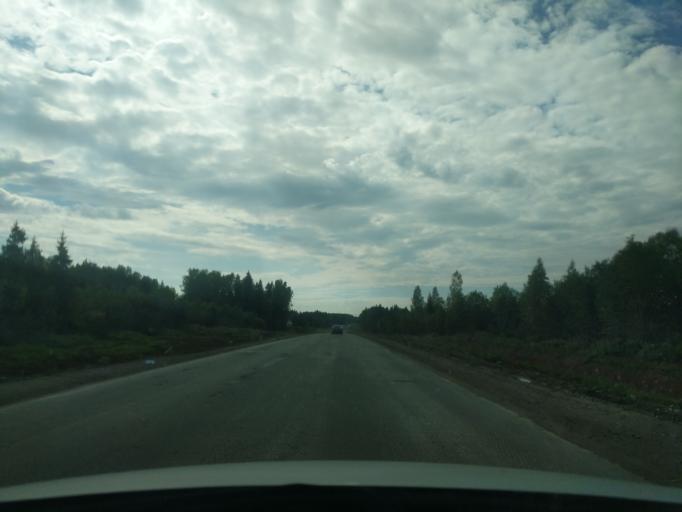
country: RU
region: Kostroma
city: Sudislavl'
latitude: 57.8548
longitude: 41.6030
